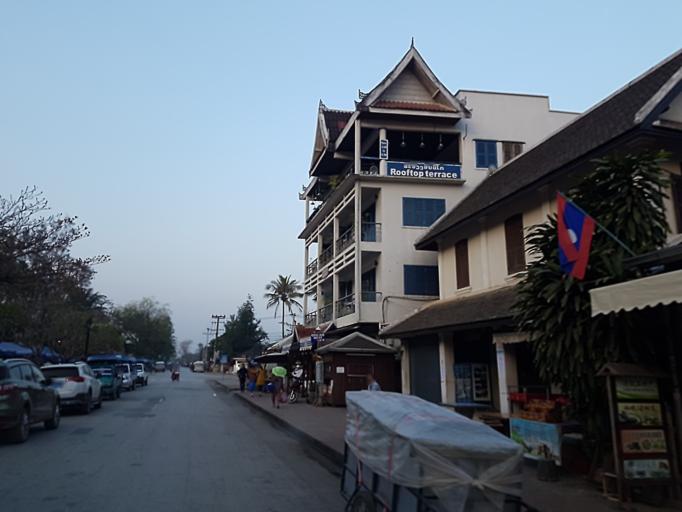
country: LA
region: Louangphabang
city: Louangphabang
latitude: 19.8897
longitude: 102.1341
